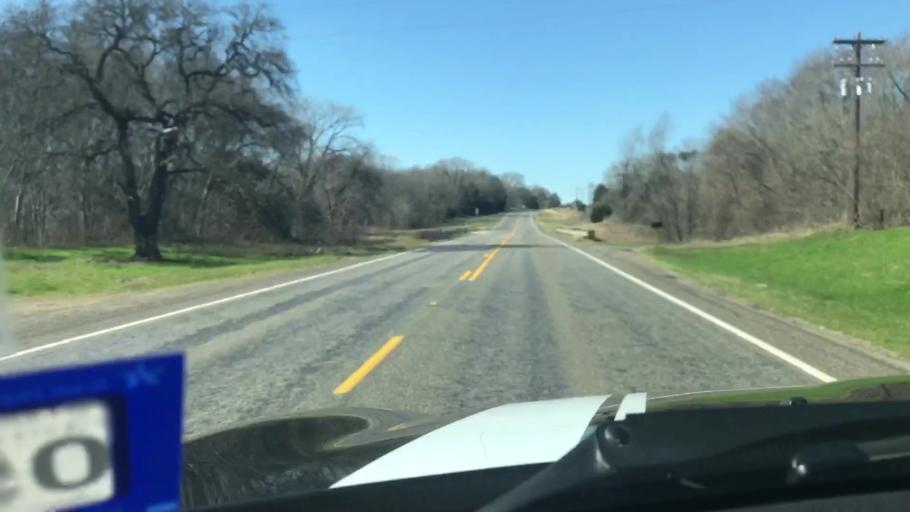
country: US
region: Texas
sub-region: Robertson County
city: Calvert
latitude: 30.8847
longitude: -96.7627
